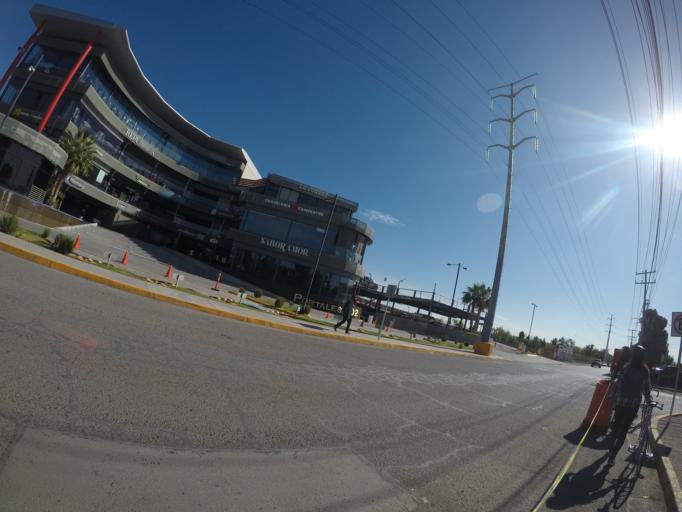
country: MX
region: Chihuahua
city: Ciudad Juarez
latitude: 31.7311
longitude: -106.4126
